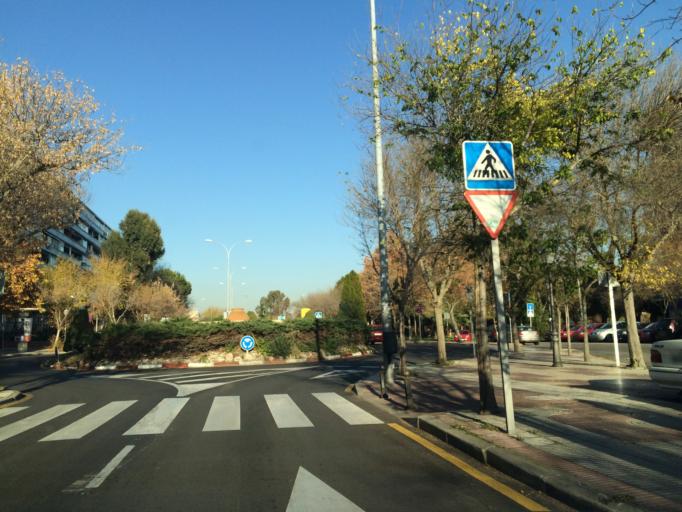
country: ES
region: Madrid
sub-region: Provincia de Madrid
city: Alcorcon
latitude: 40.3550
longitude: -3.8107
